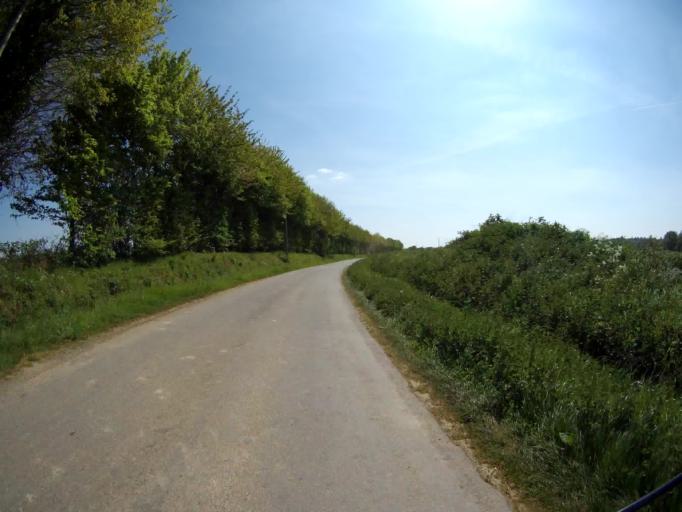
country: FR
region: Brittany
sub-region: Departement d'Ille-et-Vilaine
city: Vern-sur-Seiche
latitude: 48.0304
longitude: -1.6238
